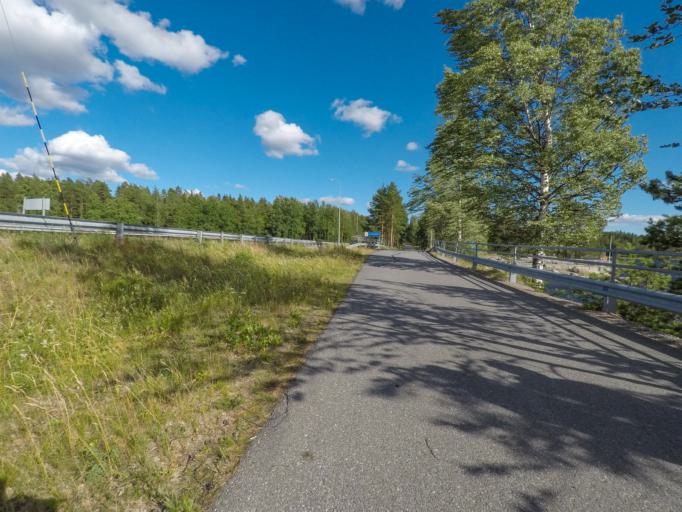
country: FI
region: South Karelia
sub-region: Lappeenranta
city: Lappeenranta
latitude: 61.0997
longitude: 28.1305
